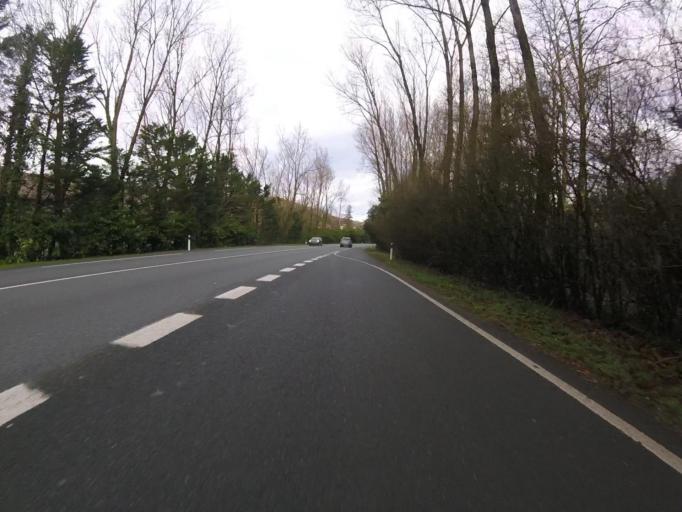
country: ES
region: Basque Country
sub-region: Provincia de Guipuzcoa
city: Irun
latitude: 43.3386
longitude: -1.8217
